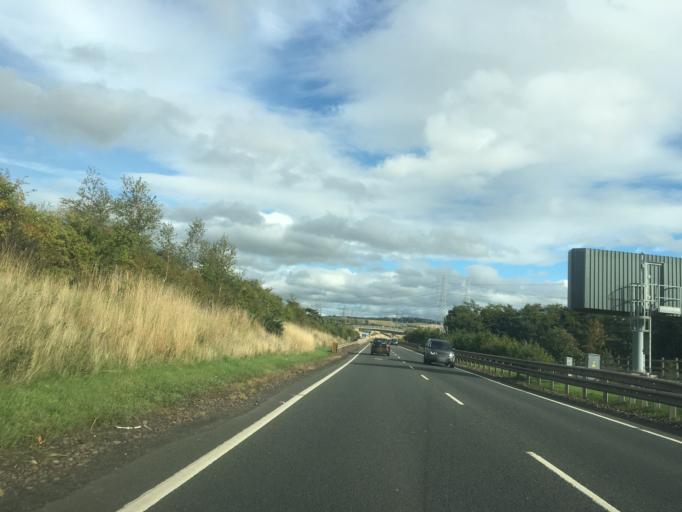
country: GB
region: Scotland
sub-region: Midlothian
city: Dalkeith
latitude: 55.9125
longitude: -3.0568
